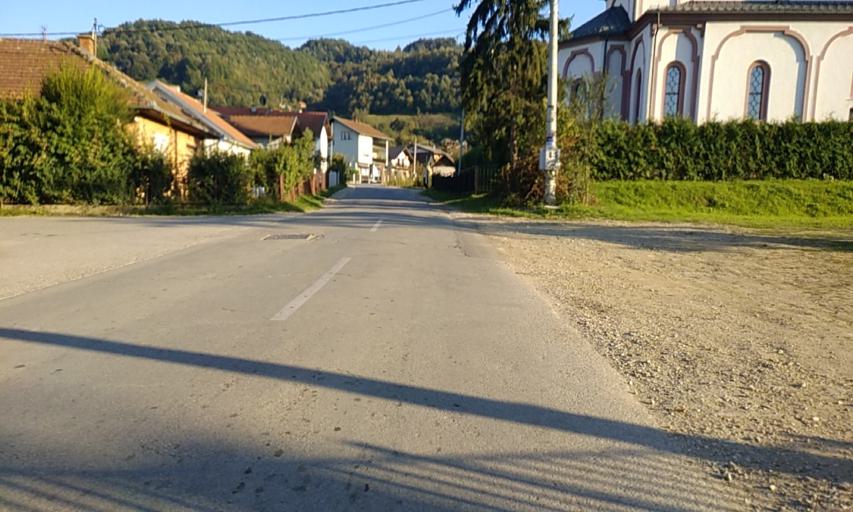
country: BA
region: Republika Srpska
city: Mejdan - Obilicevo
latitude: 44.7582
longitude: 17.1901
